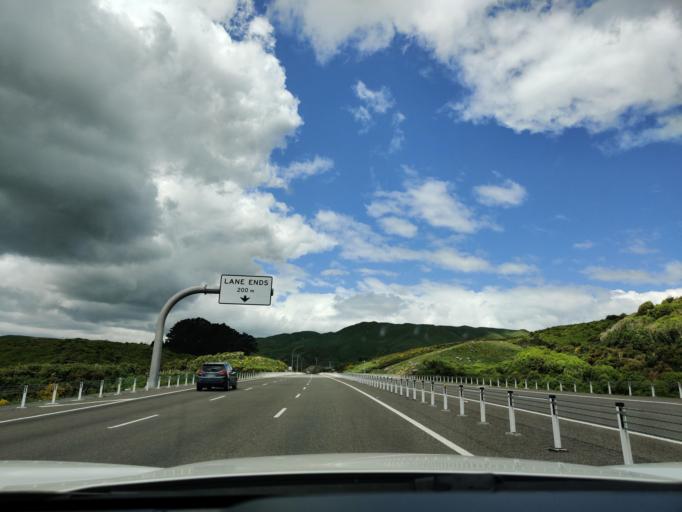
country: NZ
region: Wellington
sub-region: Porirua City
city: Porirua
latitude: -41.1541
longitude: 174.8624
